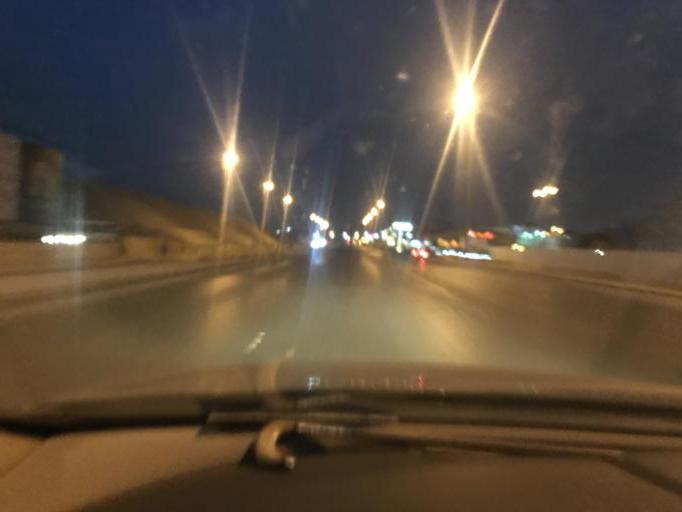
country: SA
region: Ar Riyad
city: Riyadh
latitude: 24.8140
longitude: 46.6789
